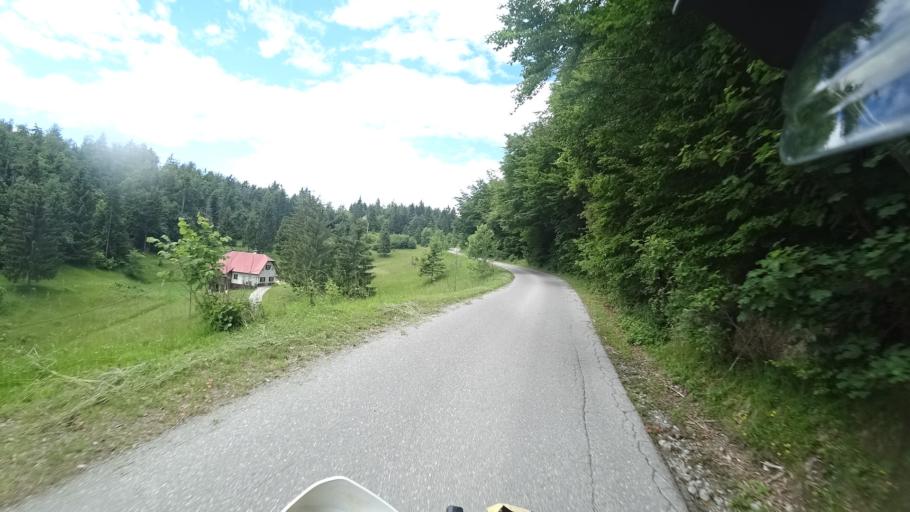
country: SI
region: Loski Potok
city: Hrib-Loski Potok
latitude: 45.6135
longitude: 14.5855
